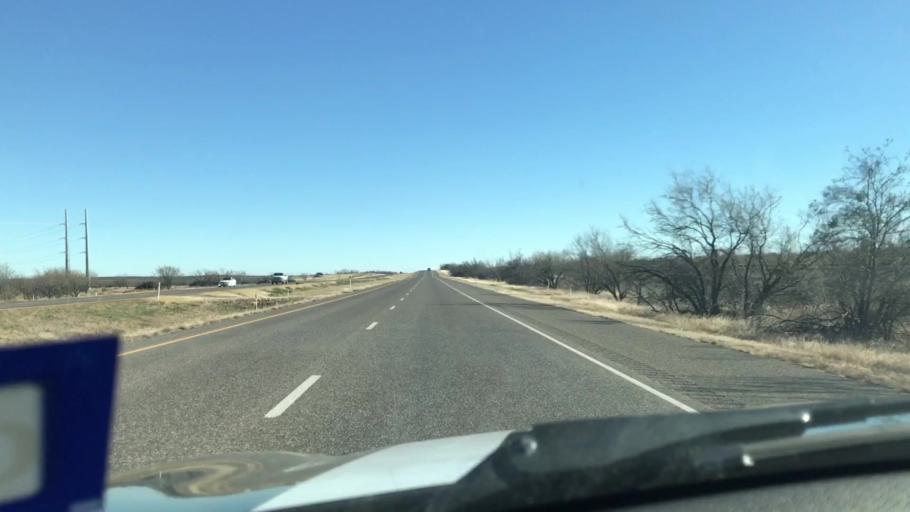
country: US
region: Texas
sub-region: Scurry County
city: Snyder
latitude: 32.8437
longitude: -101.0017
